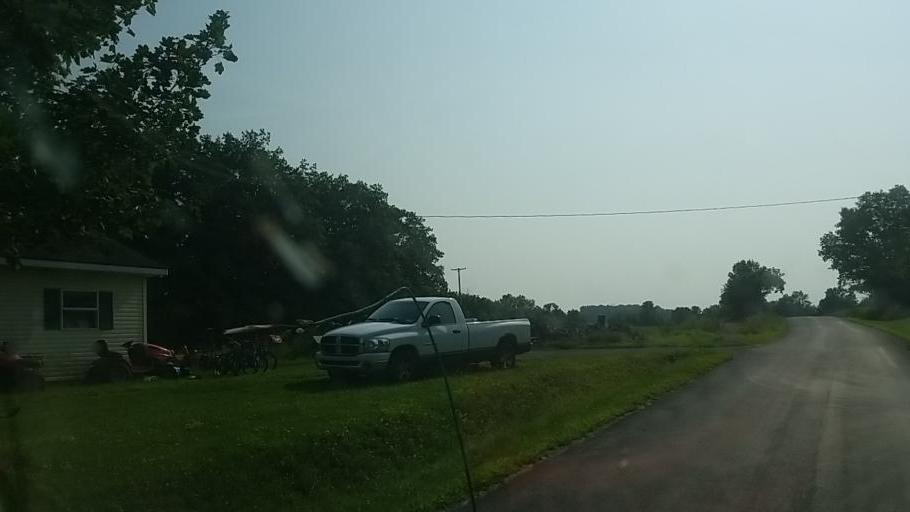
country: US
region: New York
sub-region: Montgomery County
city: Fonda
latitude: 42.9165
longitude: -74.3447
